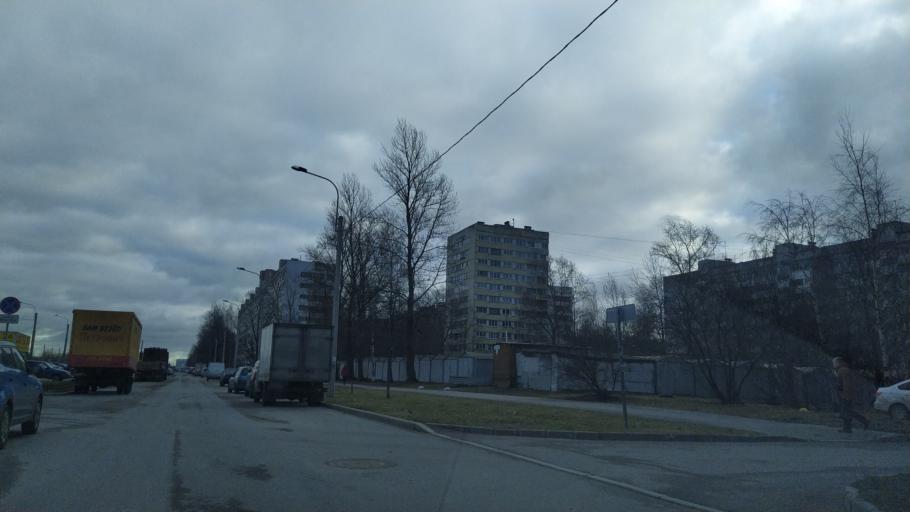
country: RU
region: Leningrad
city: Bugry
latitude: 60.0512
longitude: 30.3864
